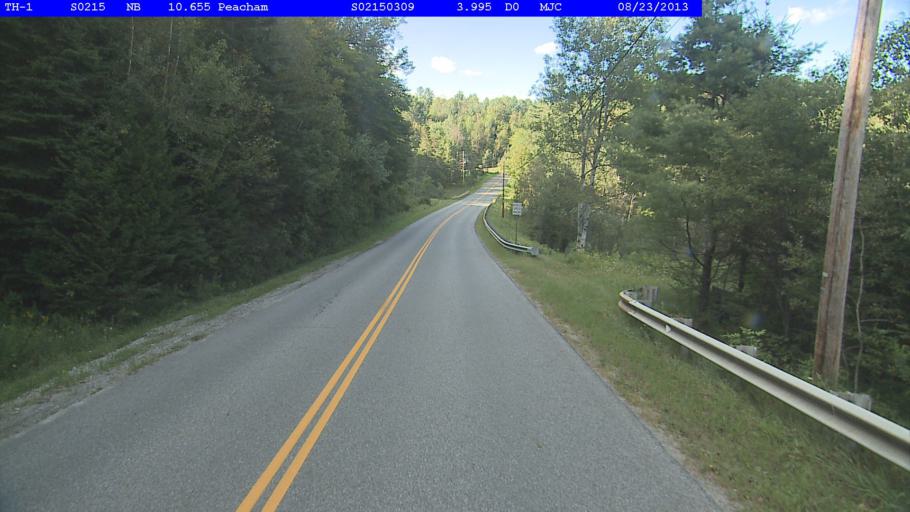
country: US
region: Vermont
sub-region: Caledonia County
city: Saint Johnsbury
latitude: 44.3538
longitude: -72.1767
